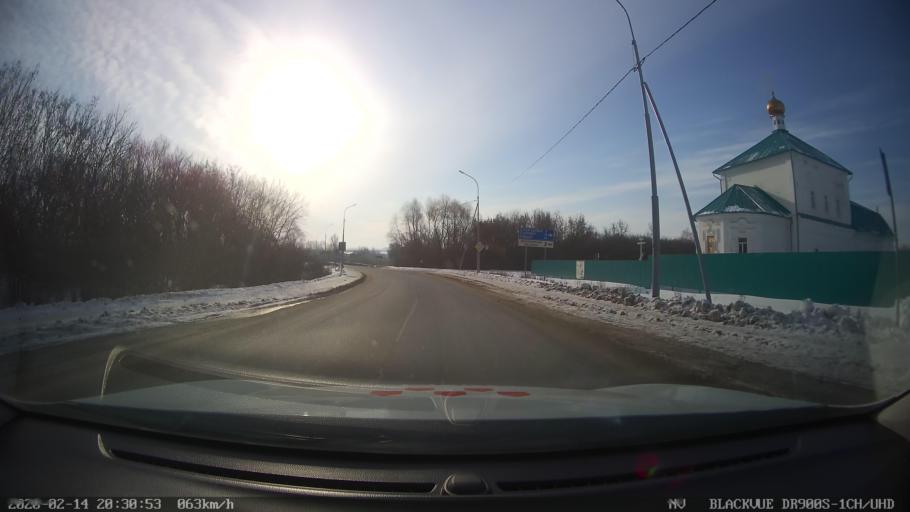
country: RU
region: Tatarstan
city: Stolbishchi
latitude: 55.4393
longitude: 48.9920
